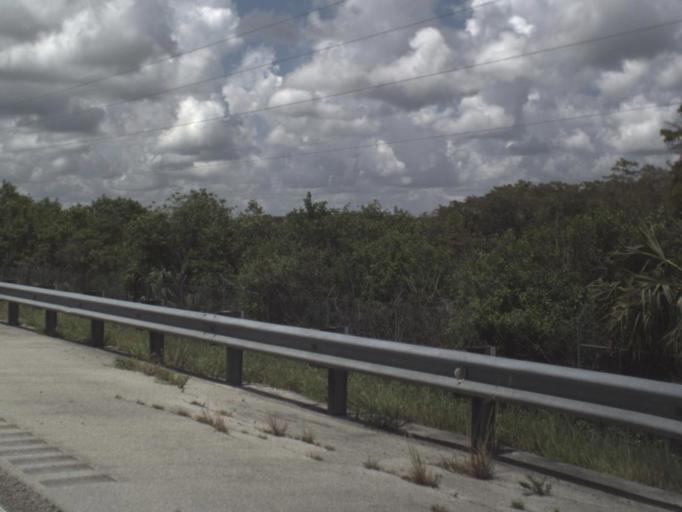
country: US
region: Florida
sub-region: Broward County
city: Weston
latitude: 26.1726
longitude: -80.8914
